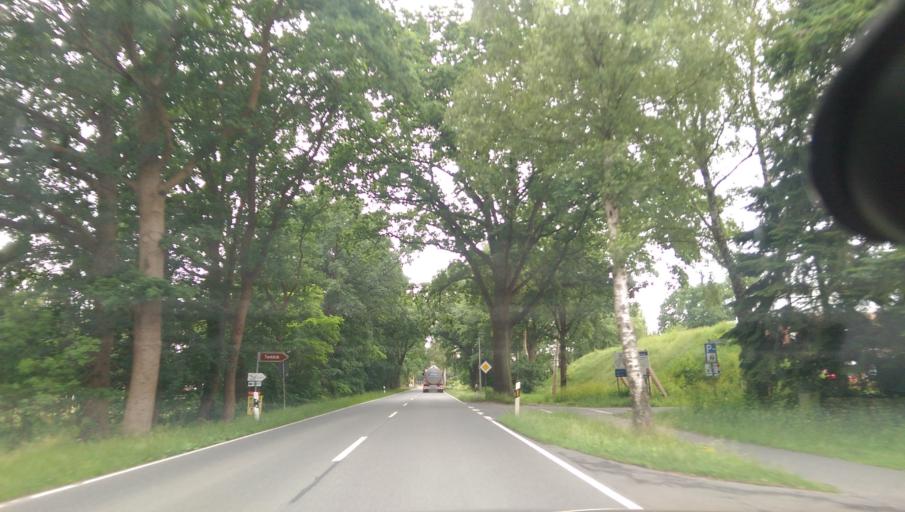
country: DE
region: Lower Saxony
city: Rotenburg
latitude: 53.0952
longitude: 9.4081
